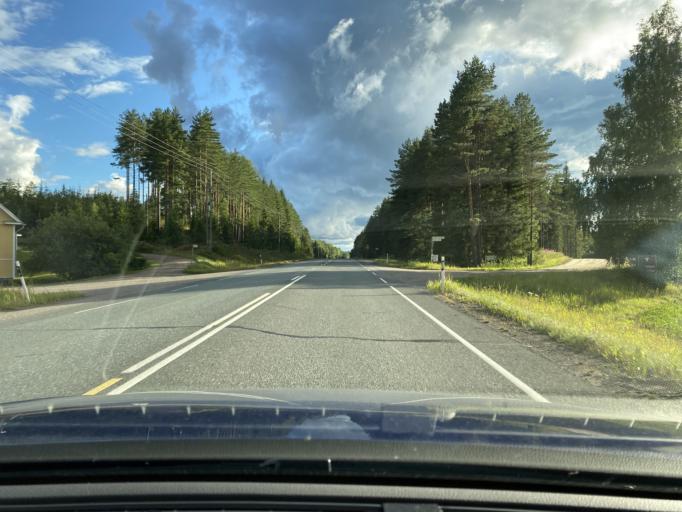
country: FI
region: Haeme
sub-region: Haemeenlinna
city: Renko
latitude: 60.8750
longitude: 24.2206
